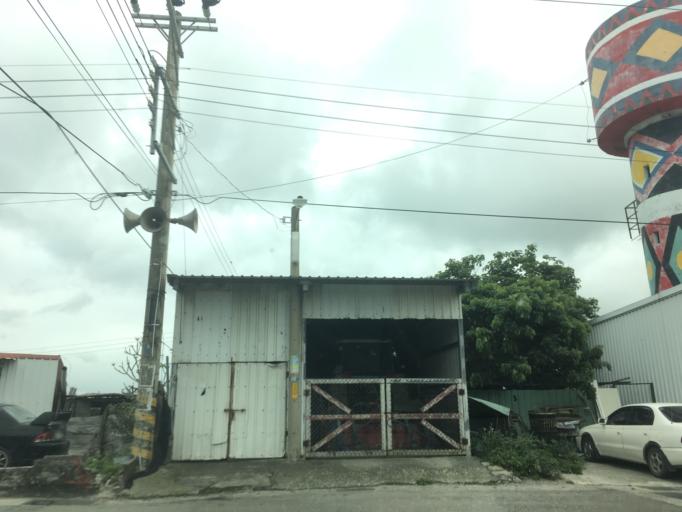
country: TW
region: Taiwan
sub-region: Taitung
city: Taitung
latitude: 22.7828
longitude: 121.1609
